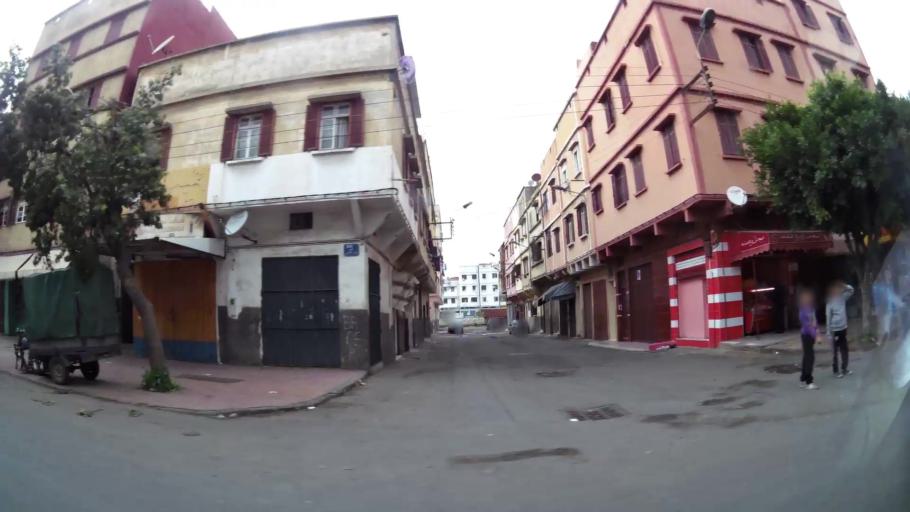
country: MA
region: Grand Casablanca
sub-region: Casablanca
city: Casablanca
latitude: 33.5566
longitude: -7.6036
